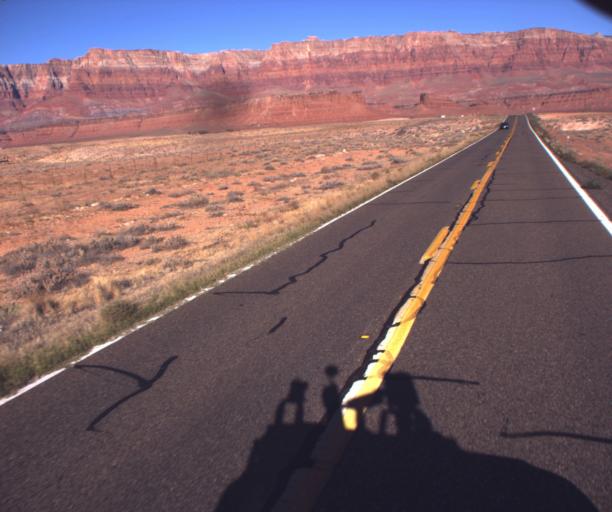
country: US
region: Arizona
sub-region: Coconino County
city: Page
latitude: 36.8056
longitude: -111.6136
